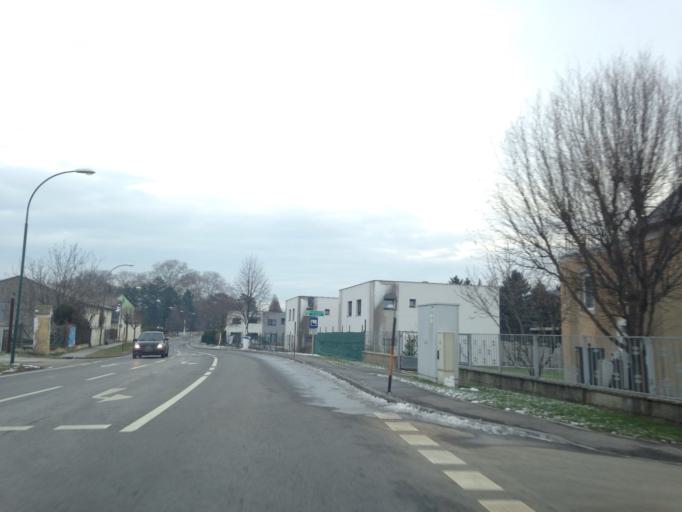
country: AT
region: Lower Austria
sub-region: Politischer Bezirk Bruck an der Leitha
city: Wolfsthal
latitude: 48.1379
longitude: 17.0007
